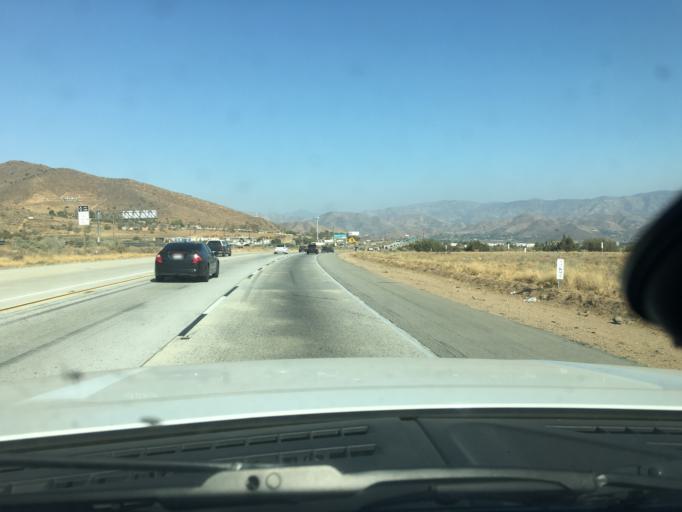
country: US
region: California
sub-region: Los Angeles County
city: Acton
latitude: 34.4996
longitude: -118.2246
